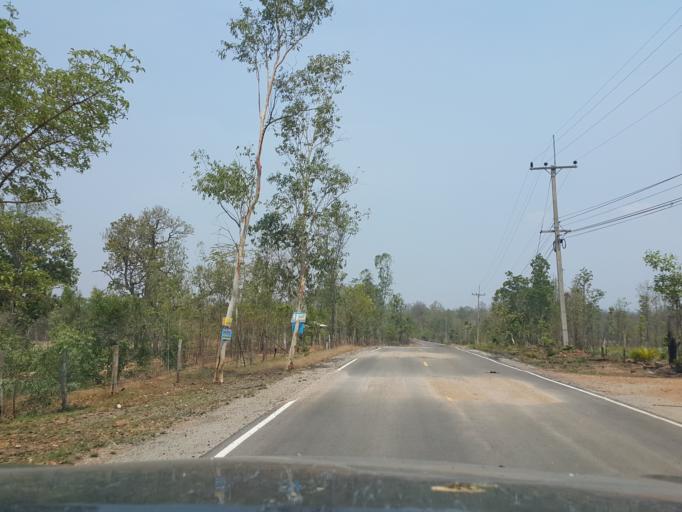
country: TH
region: Lampang
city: Mae Phrik
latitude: 17.5611
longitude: 99.0973
